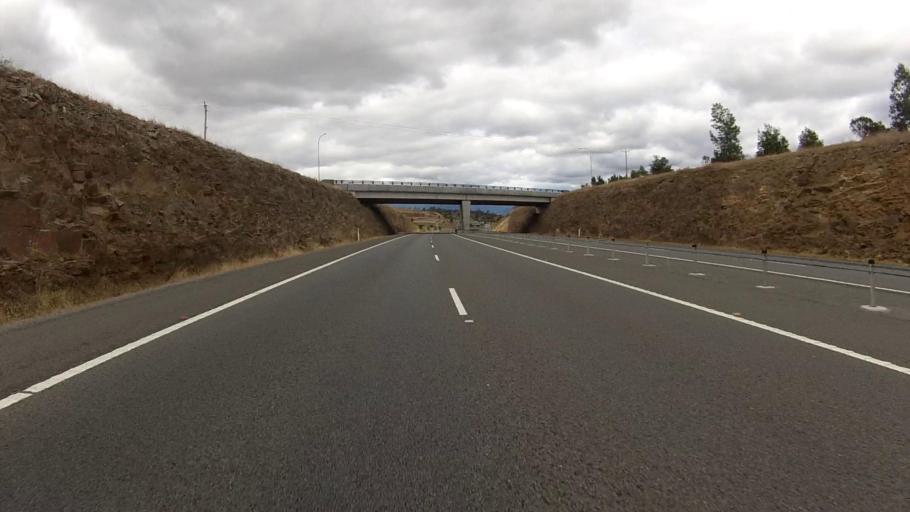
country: AU
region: Tasmania
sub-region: Brighton
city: Bridgewater
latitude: -42.6951
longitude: 147.2777
